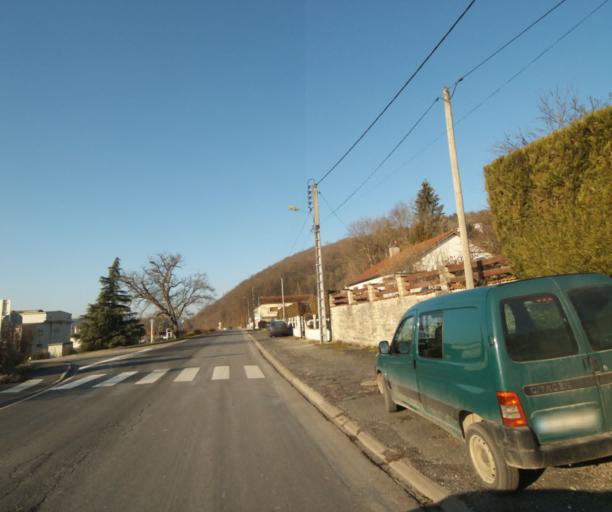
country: FR
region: Champagne-Ardenne
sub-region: Departement de la Haute-Marne
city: Chevillon
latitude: 48.5249
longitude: 5.1127
